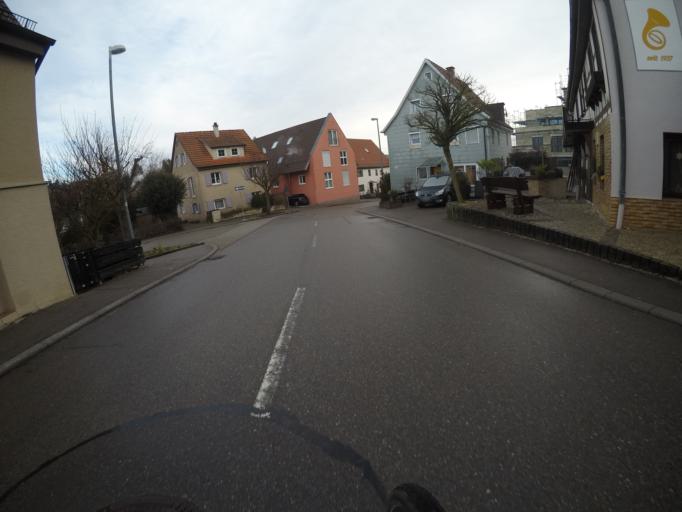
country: DE
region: Baden-Wuerttemberg
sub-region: Regierungsbezirk Stuttgart
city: Aidlingen
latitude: 48.6780
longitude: 8.8932
